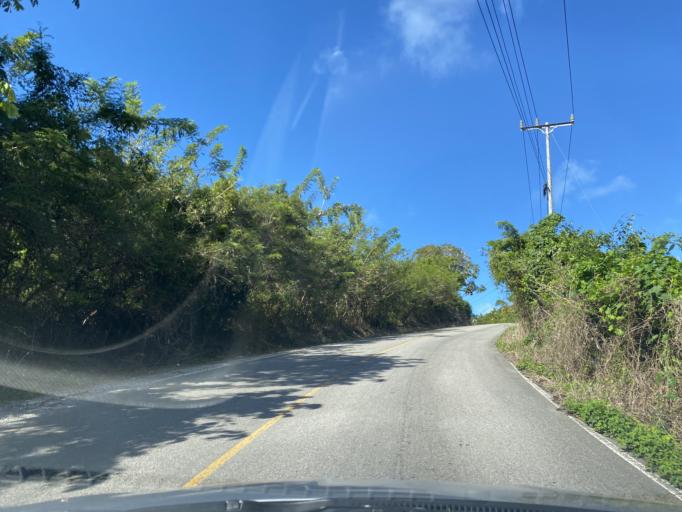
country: DO
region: Samana
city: Sanchez
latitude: 19.2446
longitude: -69.5958
